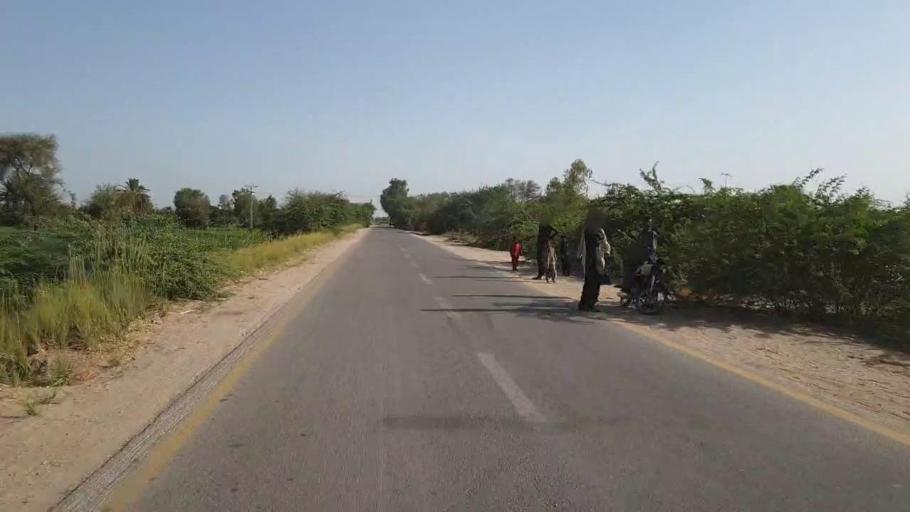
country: PK
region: Sindh
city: Daur
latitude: 26.4638
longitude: 68.4517
